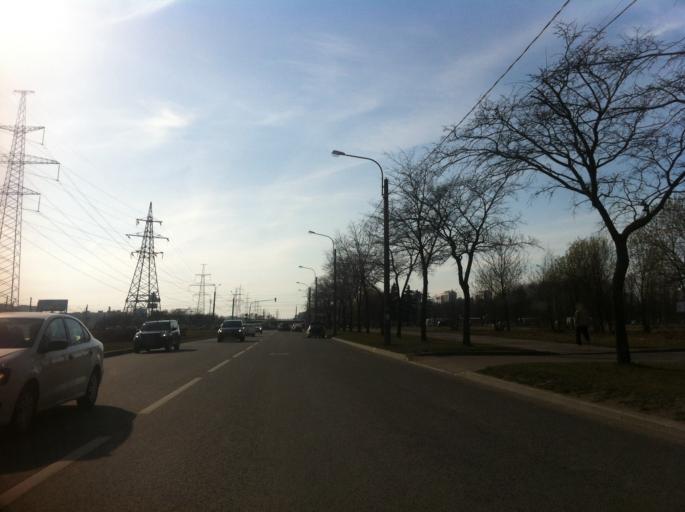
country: RU
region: St.-Petersburg
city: Uritsk
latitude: 59.8473
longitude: 30.1788
